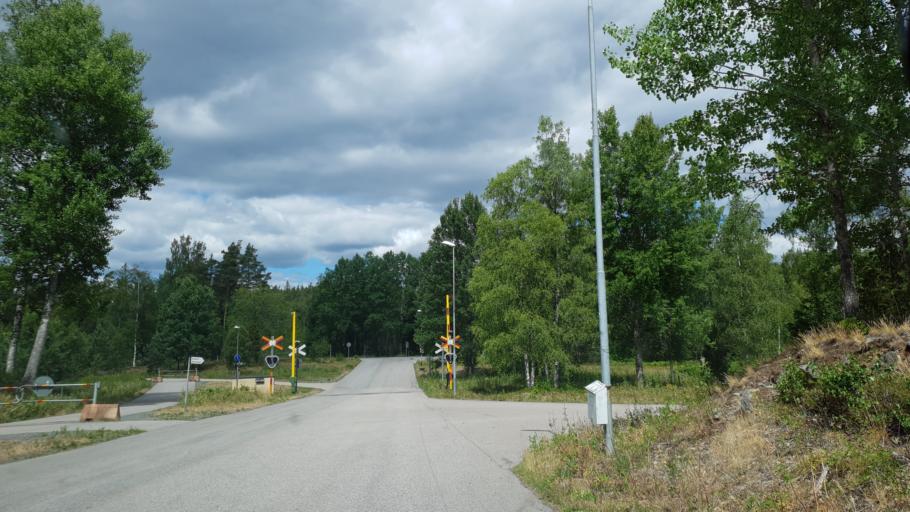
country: SE
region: Kronoberg
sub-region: Uppvidinge Kommun
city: Aseda
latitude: 57.1710
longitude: 15.3693
